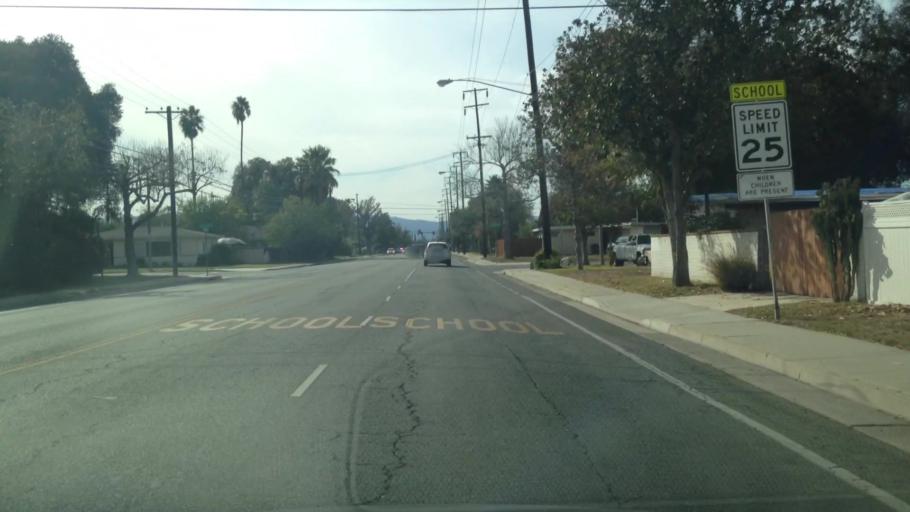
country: US
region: California
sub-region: Riverside County
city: Riverside
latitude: 33.9410
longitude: -117.4264
